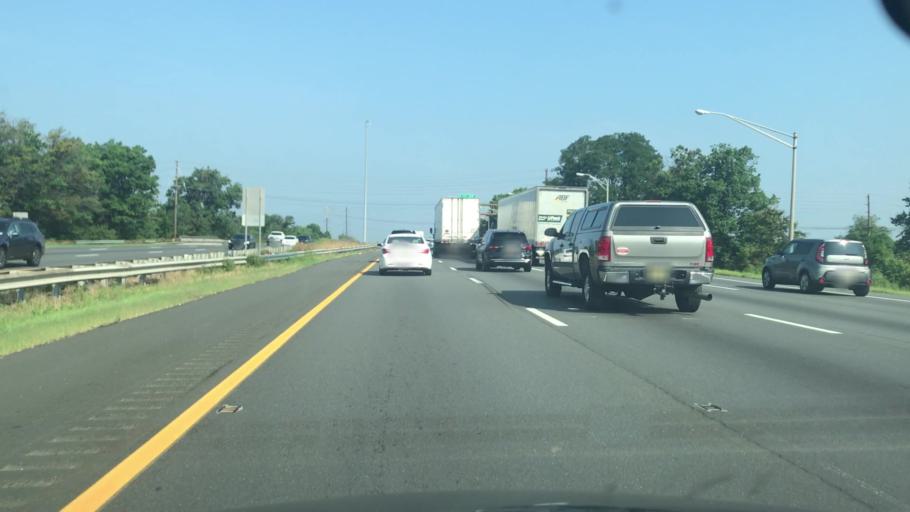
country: US
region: New Jersey
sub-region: Middlesex County
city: Metuchen
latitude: 40.5329
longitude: -74.3756
